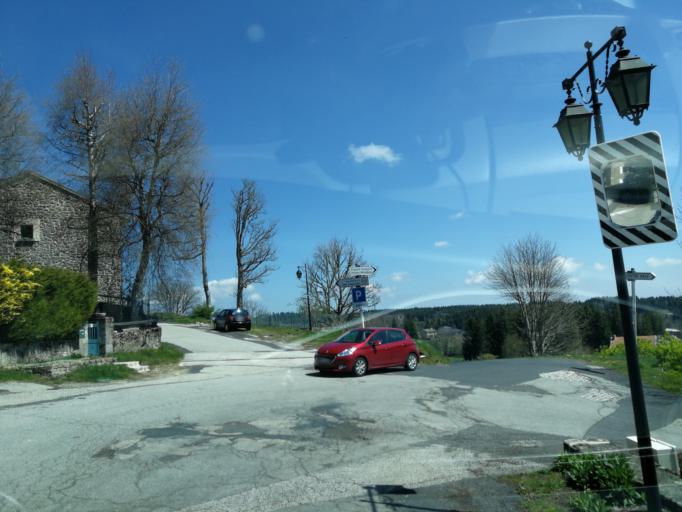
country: FR
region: Rhone-Alpes
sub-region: Departement de l'Ardeche
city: Saint-Agreve
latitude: 45.0119
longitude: 4.3965
